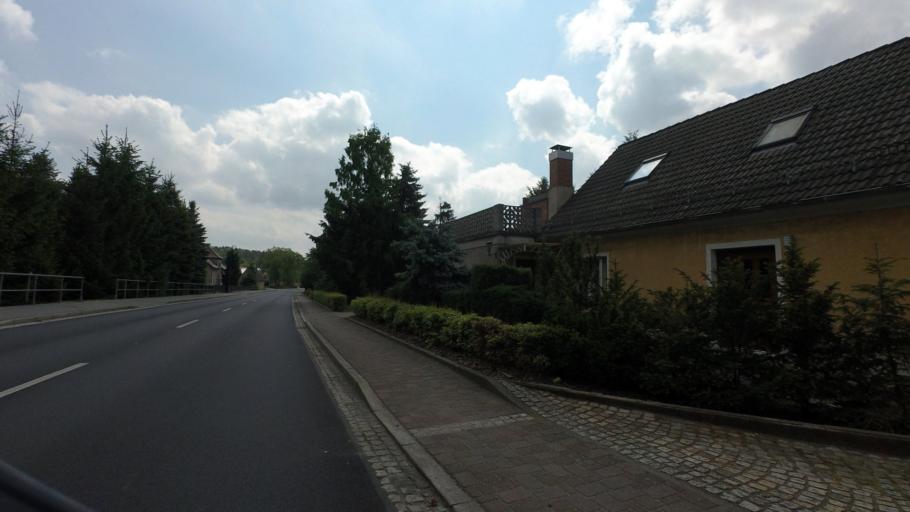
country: DE
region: Saxony
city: Rietschen
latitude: 51.3605
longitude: 14.8036
